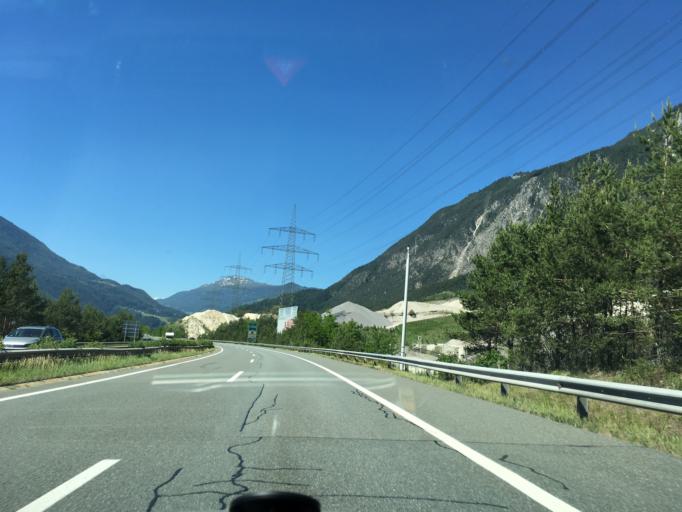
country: AT
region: Tyrol
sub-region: Politischer Bezirk Imst
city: Roppen
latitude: 47.2355
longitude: 10.8388
